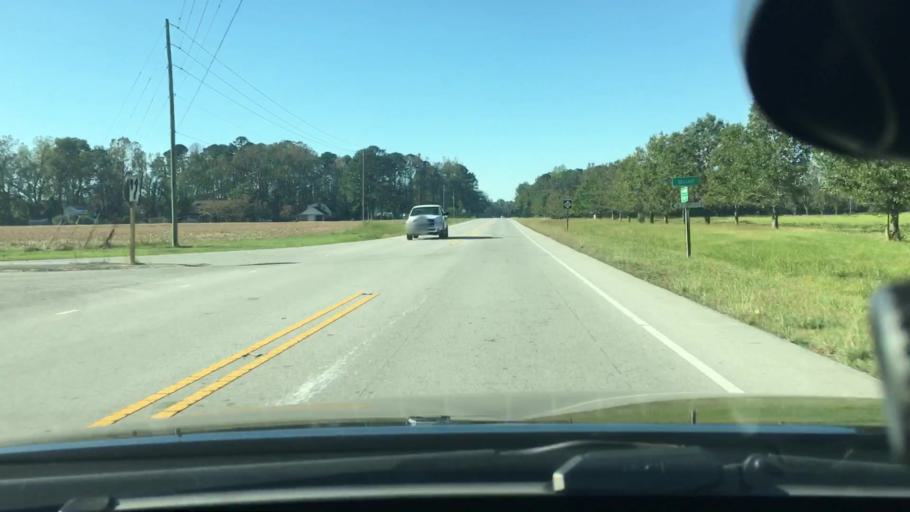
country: US
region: North Carolina
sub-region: Craven County
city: Trent Woods
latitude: 35.1656
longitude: -77.1214
